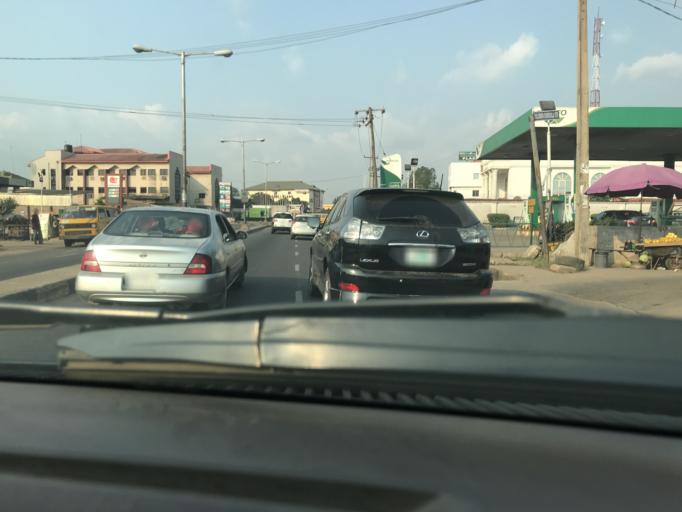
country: NG
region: Lagos
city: Ikotun
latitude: 6.5834
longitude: 3.2836
